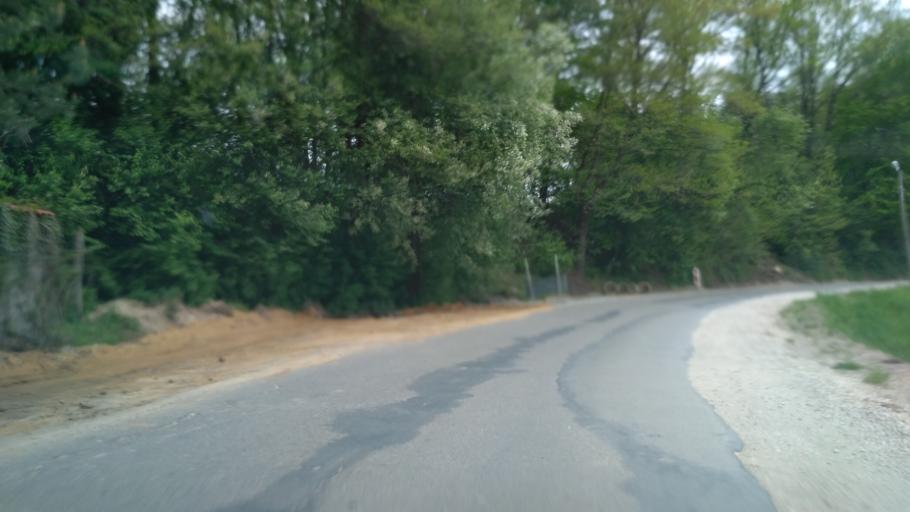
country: PL
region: Lesser Poland Voivodeship
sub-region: Powiat tarnowski
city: Skrzyszow
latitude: 49.9860
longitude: 21.0619
